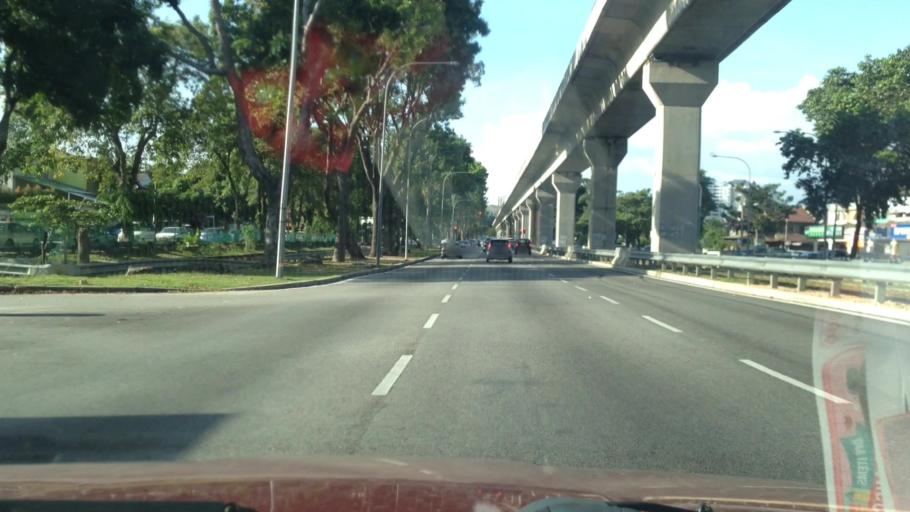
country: MY
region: Selangor
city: Subang Jaya
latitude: 3.0375
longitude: 101.5881
